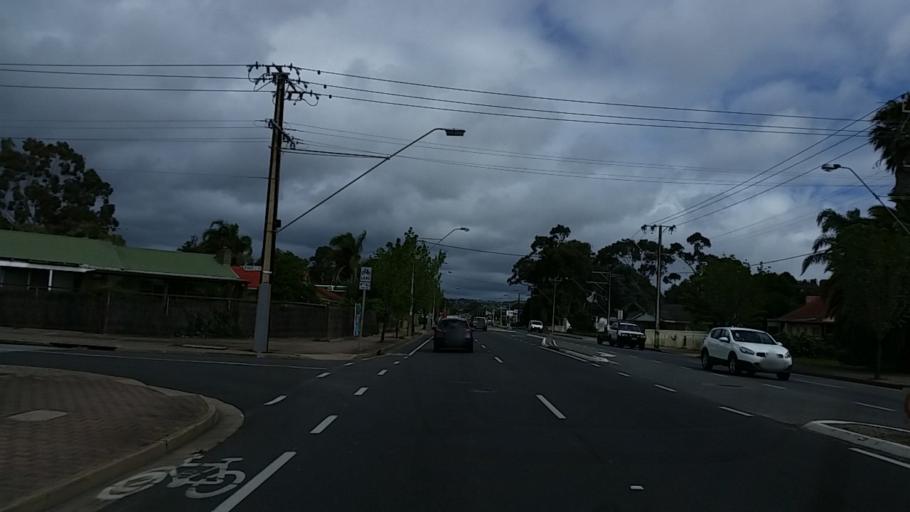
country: AU
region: South Australia
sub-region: Marion
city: Clovelly Park
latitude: -35.0012
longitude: 138.5577
